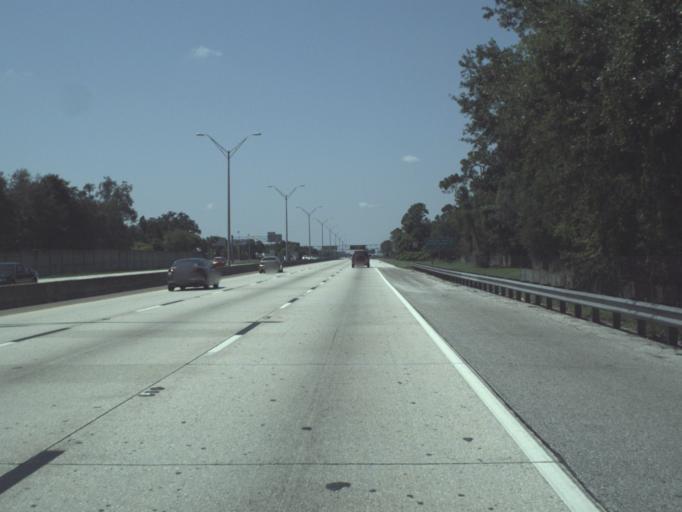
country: US
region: Florida
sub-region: Hillsborough County
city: Lake Magdalene
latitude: 28.0809
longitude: -82.4549
